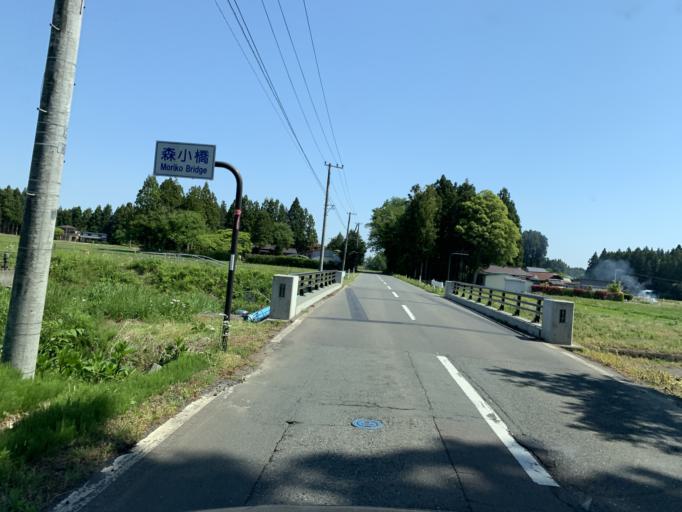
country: JP
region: Iwate
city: Mizusawa
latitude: 39.0852
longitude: 141.0680
